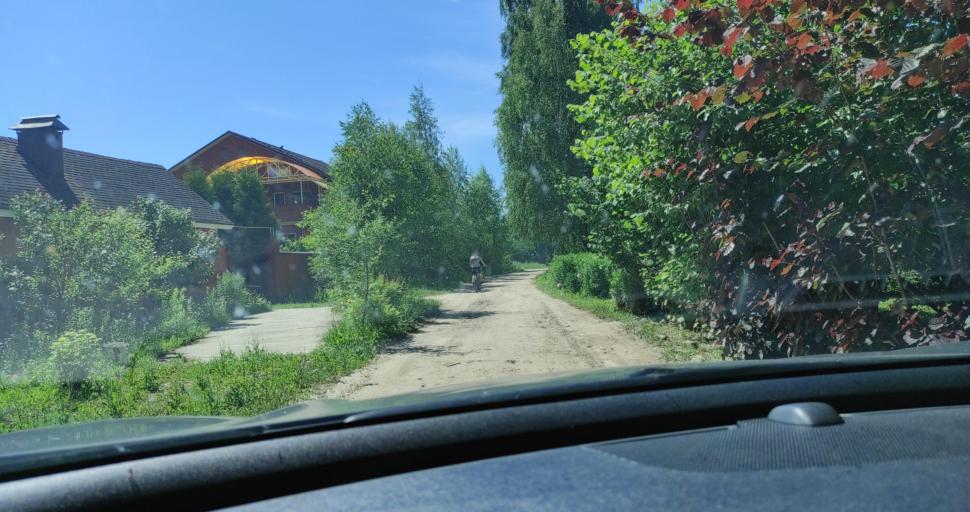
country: RU
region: Rjazan
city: Murmino
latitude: 54.5604
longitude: 40.0949
